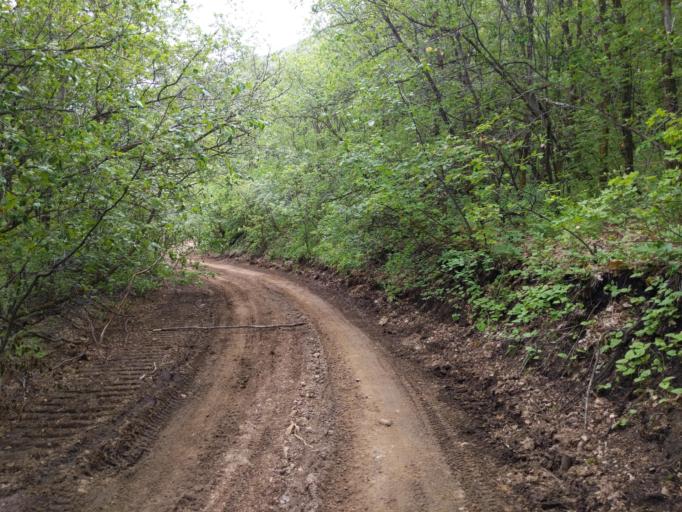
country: US
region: Idaho
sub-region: Bannock County
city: Pocatello
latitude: 42.8230
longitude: -112.4844
